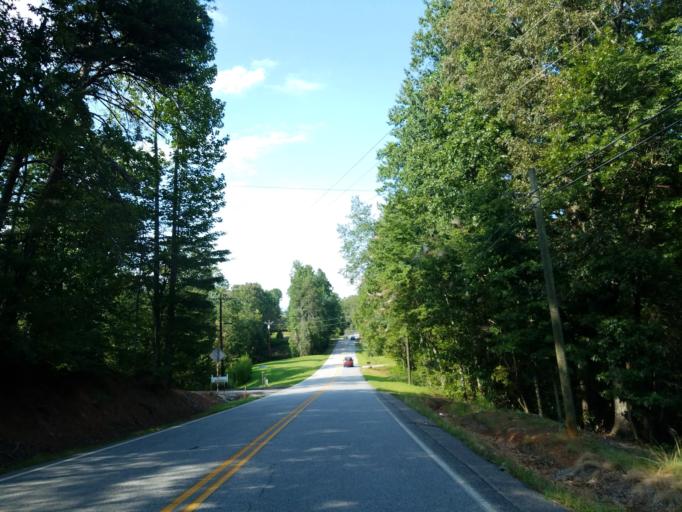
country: US
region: Georgia
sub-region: Lumpkin County
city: Dahlonega
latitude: 34.5971
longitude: -83.9707
